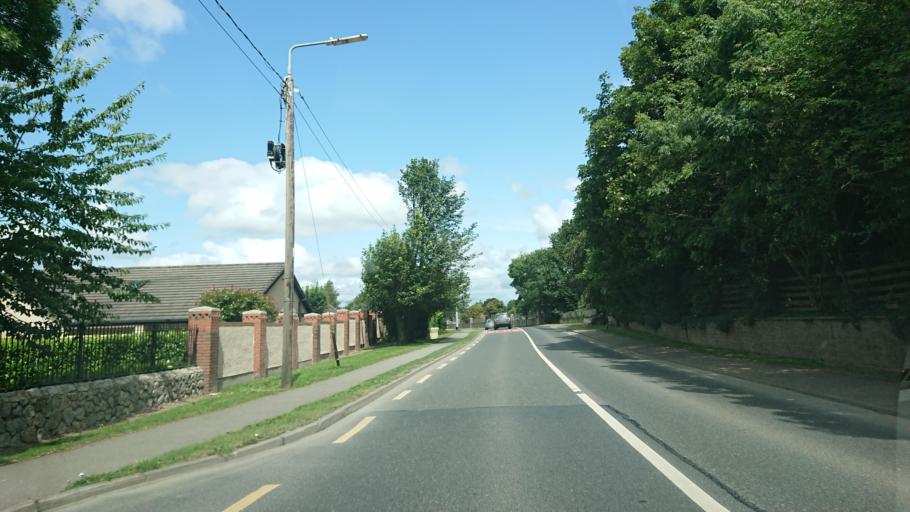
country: IE
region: Leinster
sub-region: Kildare
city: Sallins
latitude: 53.2547
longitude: -6.6675
